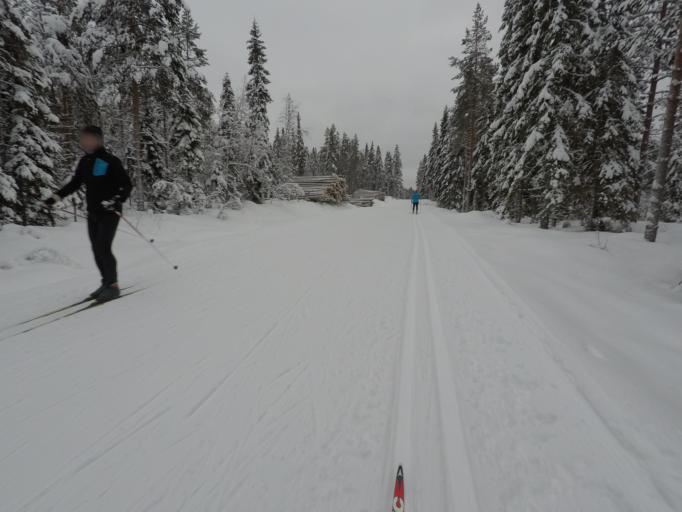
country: SE
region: Dalarna
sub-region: Ludvika Kommun
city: Abborrberget
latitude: 60.1587
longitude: 14.4892
